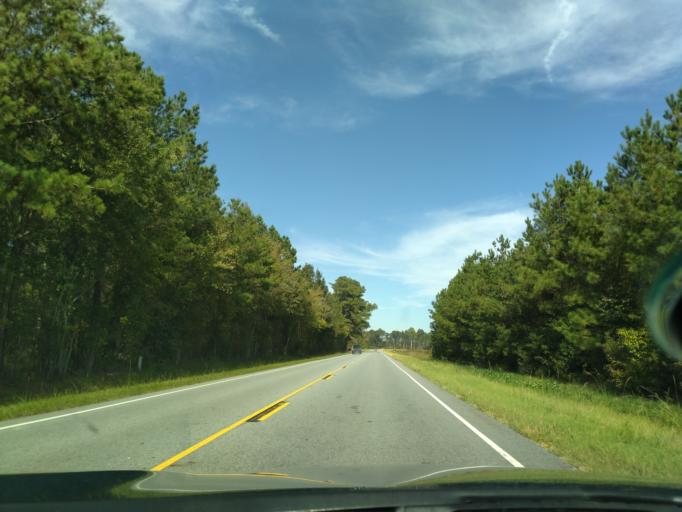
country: US
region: North Carolina
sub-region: Beaufort County
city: River Road
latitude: 35.5167
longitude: -76.8956
